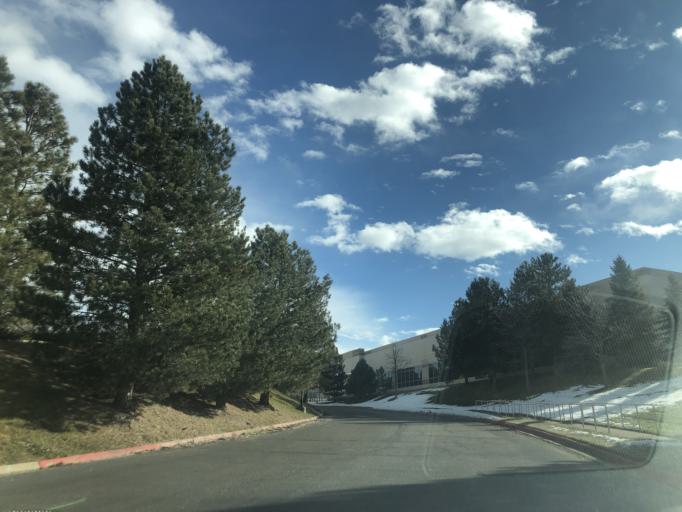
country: US
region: Colorado
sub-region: Douglas County
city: Meridian
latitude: 39.5598
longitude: -104.8591
